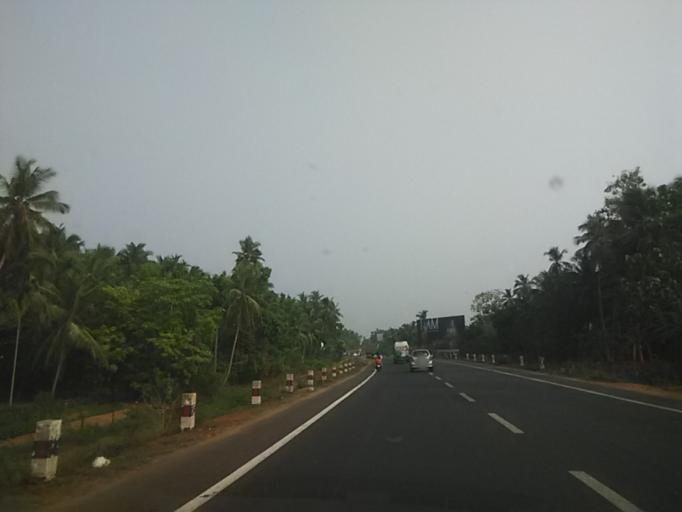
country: IN
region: Kerala
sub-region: Kozhikode
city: Kozhikode
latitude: 11.3133
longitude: 75.7813
